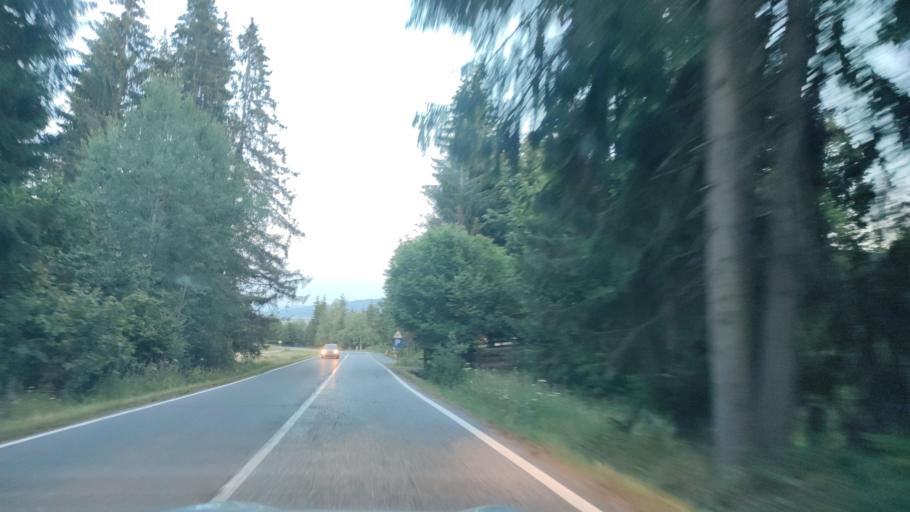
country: RO
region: Harghita
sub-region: Comuna Remetea
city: Remetea
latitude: 46.6762
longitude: 25.3656
